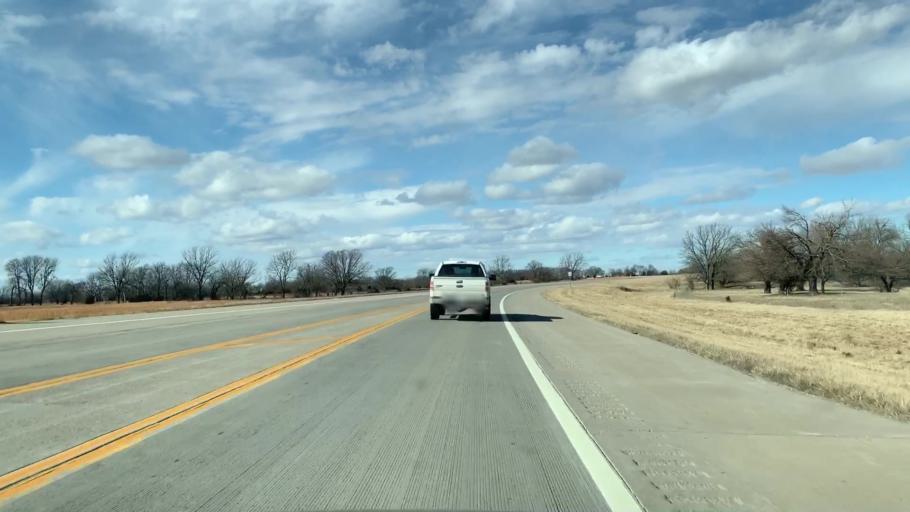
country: US
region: Kansas
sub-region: Labette County
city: Parsons
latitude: 37.3427
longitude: -95.1823
